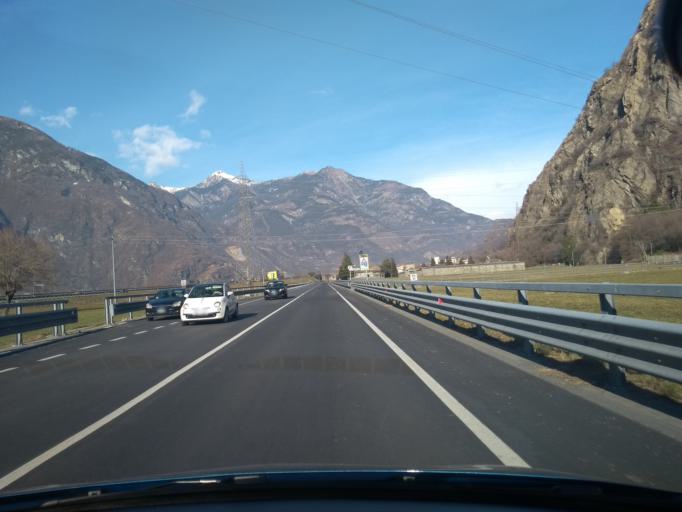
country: IT
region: Aosta Valley
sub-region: Valle d'Aosta
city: Issogne
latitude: 45.6554
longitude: 7.6988
